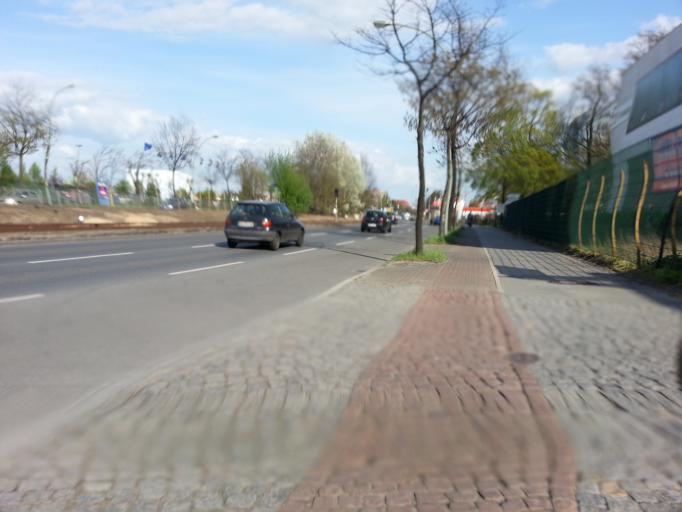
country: DE
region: Berlin
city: Haselhorst
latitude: 52.5383
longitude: 13.2431
